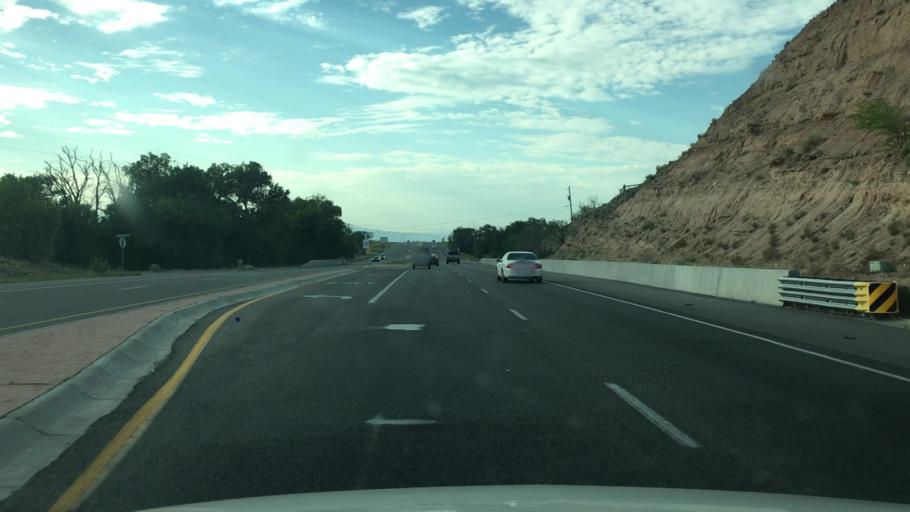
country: US
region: New Mexico
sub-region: Santa Fe County
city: El Valle de Arroyo Seco
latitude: 35.9836
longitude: -106.0505
